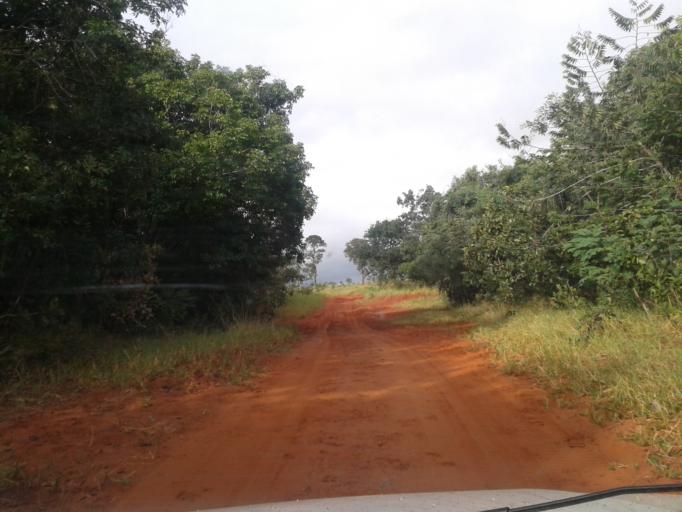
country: BR
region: Minas Gerais
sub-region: Campina Verde
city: Campina Verde
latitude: -19.4076
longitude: -49.6347
